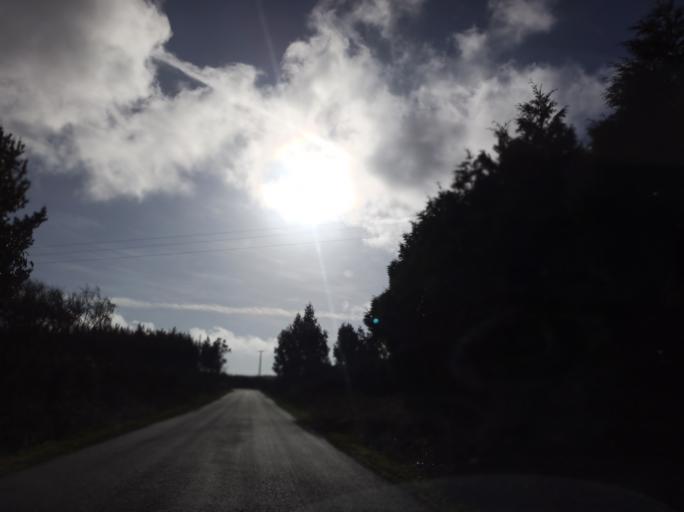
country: ES
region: Galicia
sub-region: Provincia da Coruna
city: Sobrado
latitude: 43.0827
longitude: -7.9615
